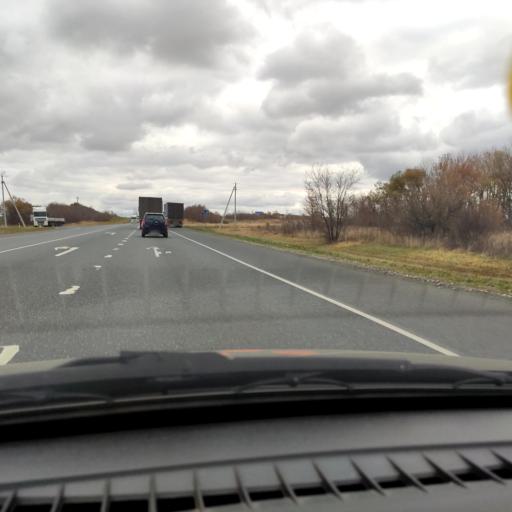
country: RU
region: Samara
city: Mezhdurechensk
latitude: 53.2448
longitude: 48.9920
